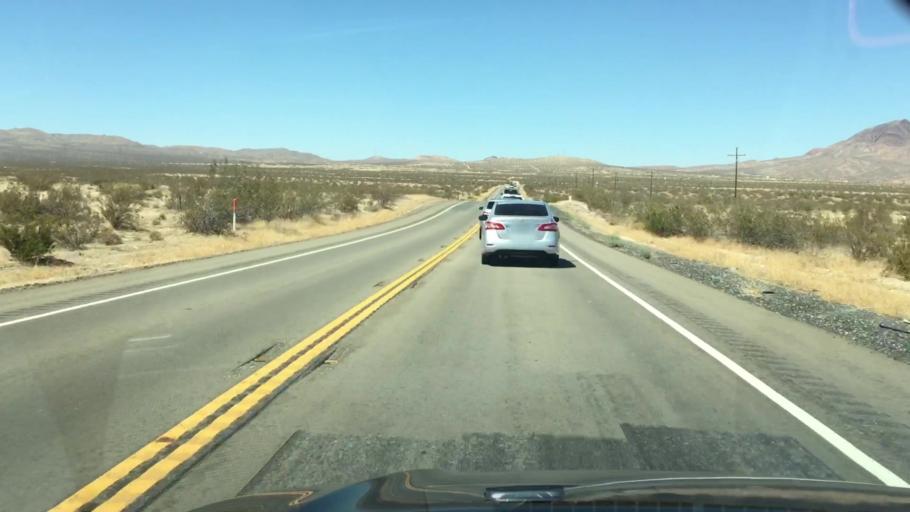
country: US
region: California
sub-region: Kern County
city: Boron
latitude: 35.2800
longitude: -117.6155
